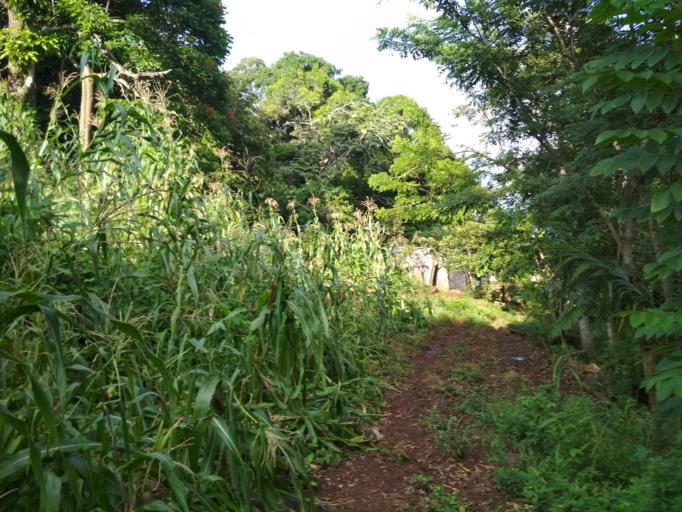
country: MX
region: Veracruz
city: Catemaco
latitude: 18.3883
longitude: -95.1246
